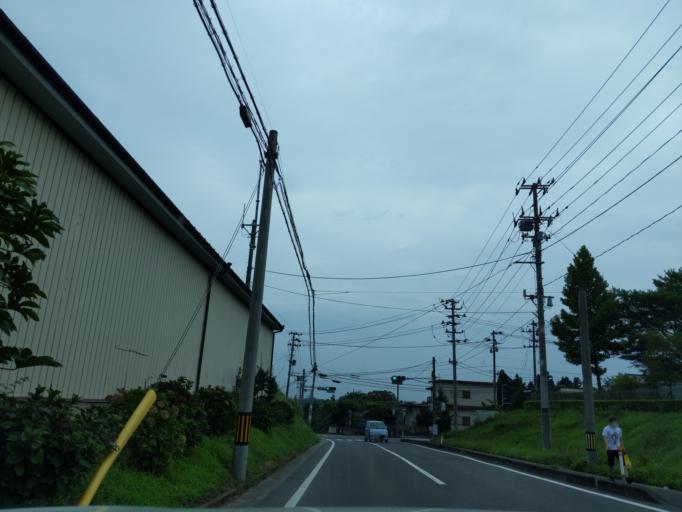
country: JP
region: Fukushima
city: Sukagawa
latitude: 37.3121
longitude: 140.3721
